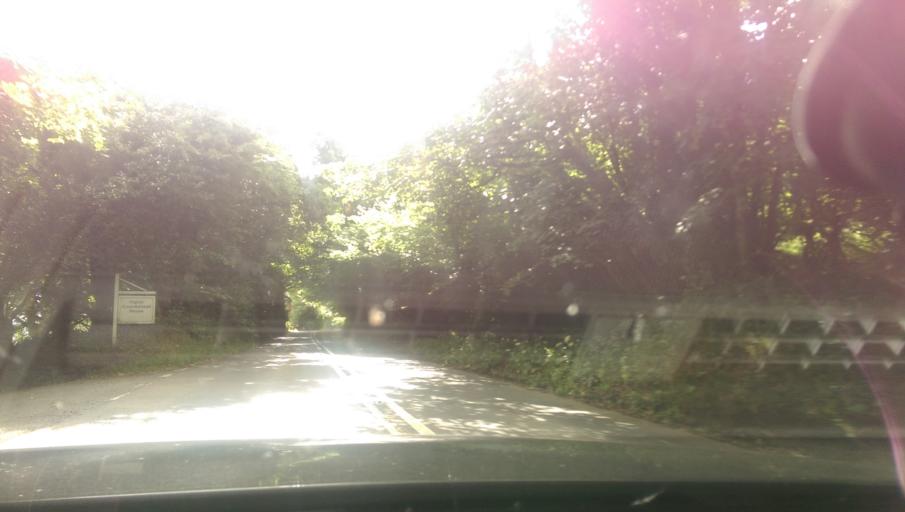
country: GB
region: England
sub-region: Devon
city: Okehampton
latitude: 50.7367
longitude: -3.9484
